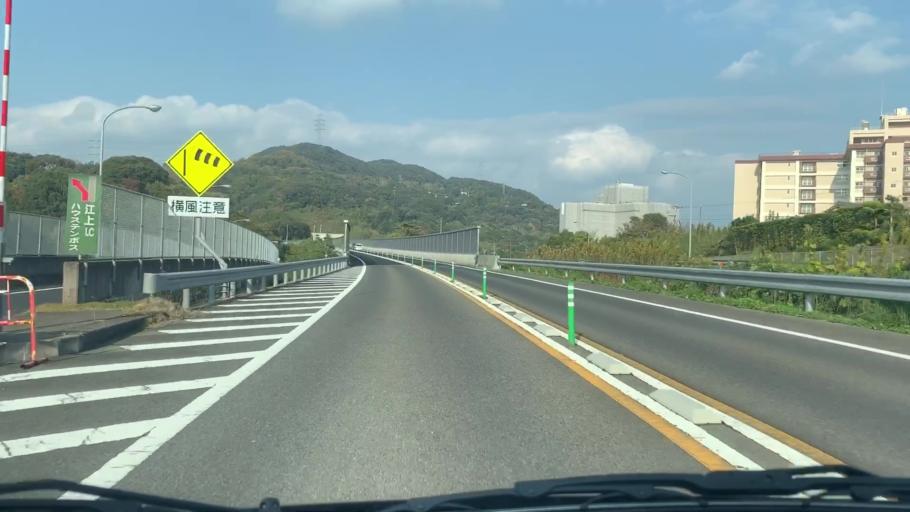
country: JP
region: Nagasaki
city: Sasebo
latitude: 33.0820
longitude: 129.7761
